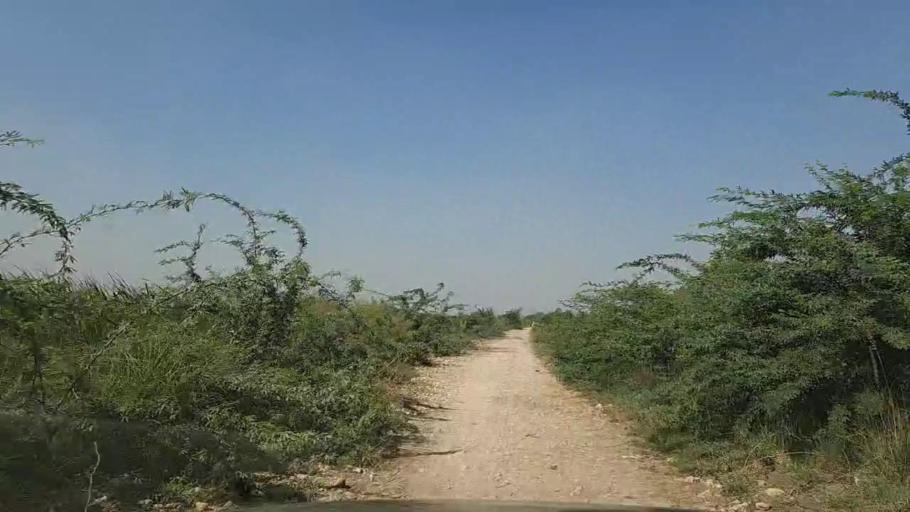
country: PK
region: Sindh
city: Daro Mehar
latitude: 24.8165
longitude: 68.1516
